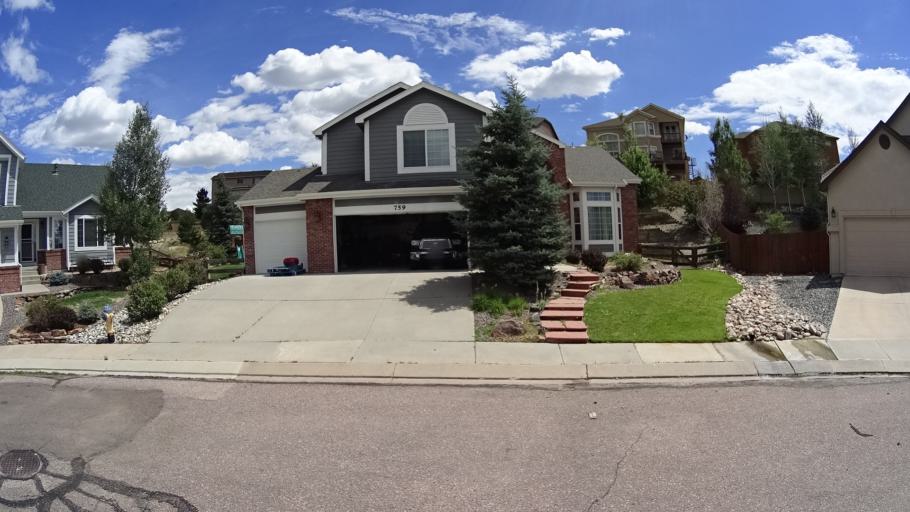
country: US
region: Colorado
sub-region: El Paso County
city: Gleneagle
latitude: 39.0295
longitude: -104.8154
